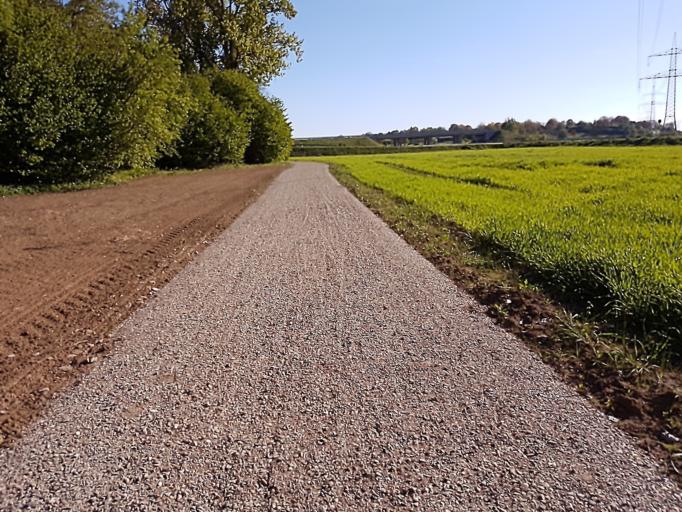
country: DE
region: Baden-Wuerttemberg
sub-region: Freiburg Region
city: Gottenheim
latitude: 48.0589
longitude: 7.7252
